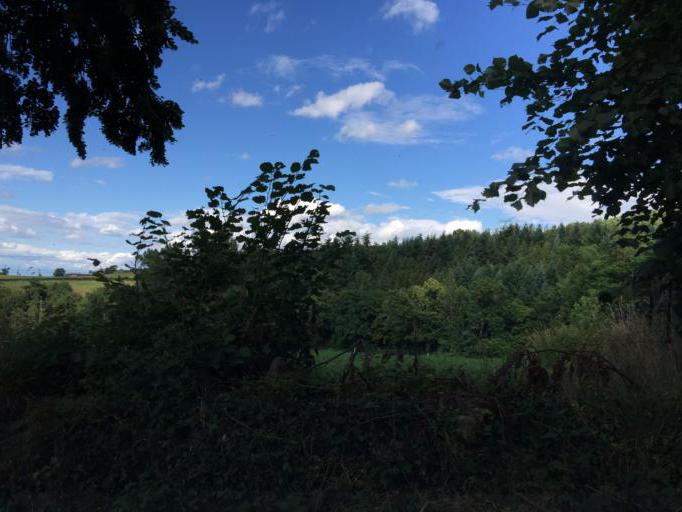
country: FR
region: Rhone-Alpes
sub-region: Departement de la Loire
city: Saint-Jean-Bonnefonds
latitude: 45.4422
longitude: 4.4785
